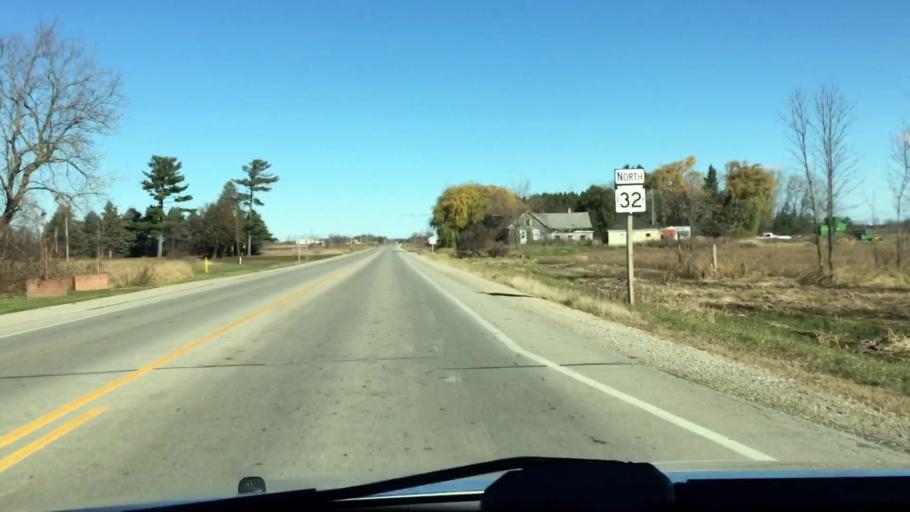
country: US
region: Wisconsin
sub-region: Brown County
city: Pulaski
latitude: 44.7164
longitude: -88.2453
